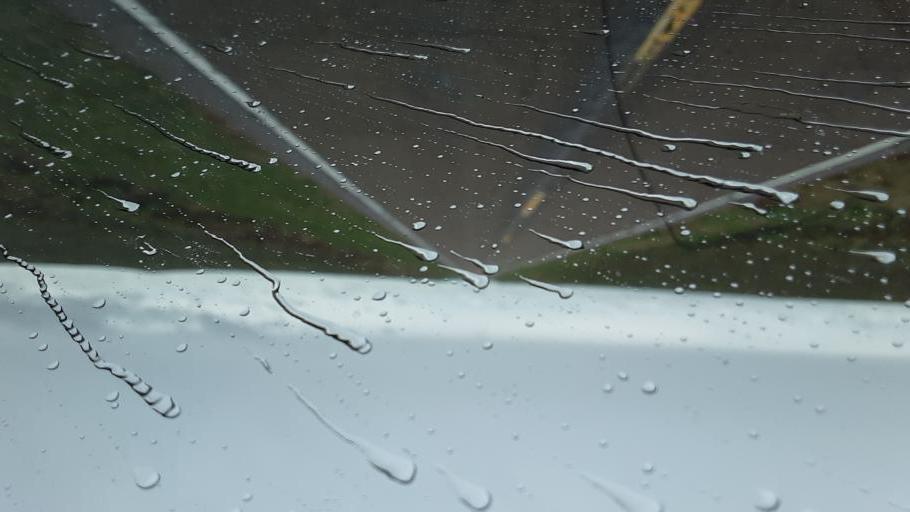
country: US
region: Colorado
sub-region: Lincoln County
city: Hugo
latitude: 38.8494
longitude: -103.2333
